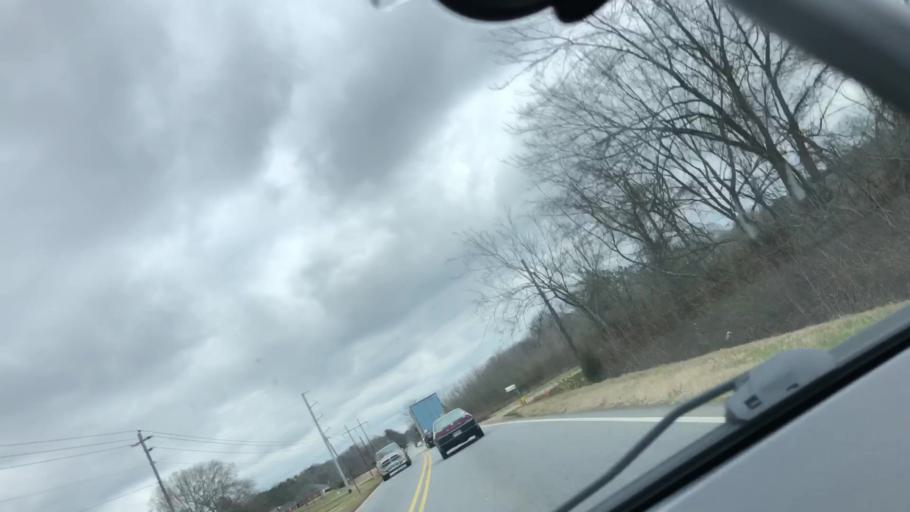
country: US
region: Georgia
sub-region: Bartow County
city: Cartersville
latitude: 34.1712
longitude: -84.8291
